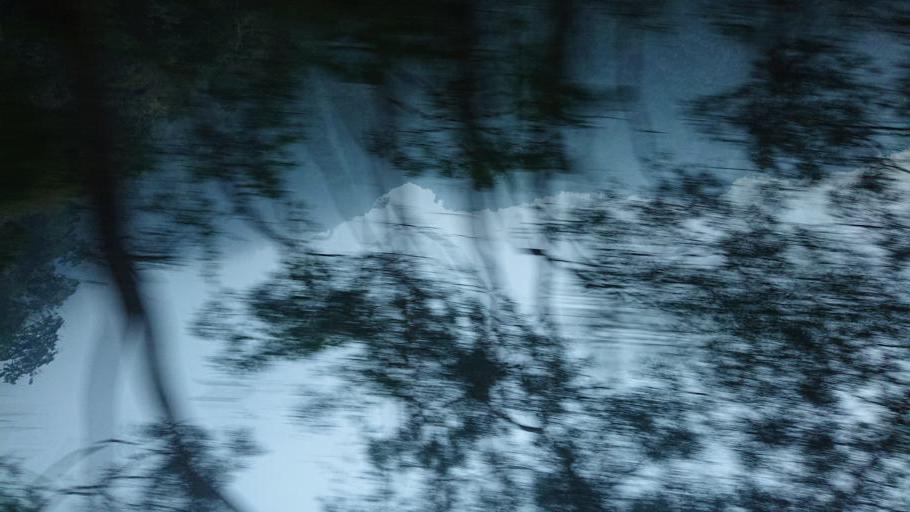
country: TW
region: Taiwan
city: Lugu
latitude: 23.5952
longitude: 120.7240
